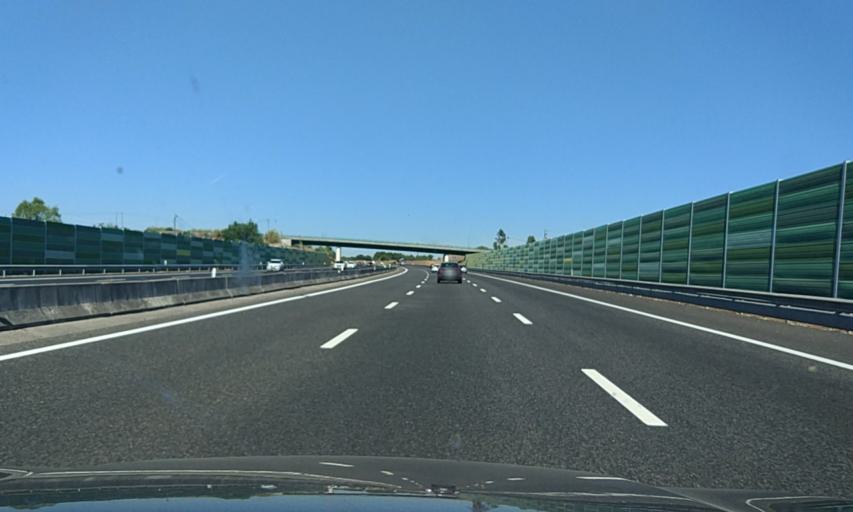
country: PT
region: Santarem
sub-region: Cartaxo
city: Pontevel
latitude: 39.1767
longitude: -8.8379
